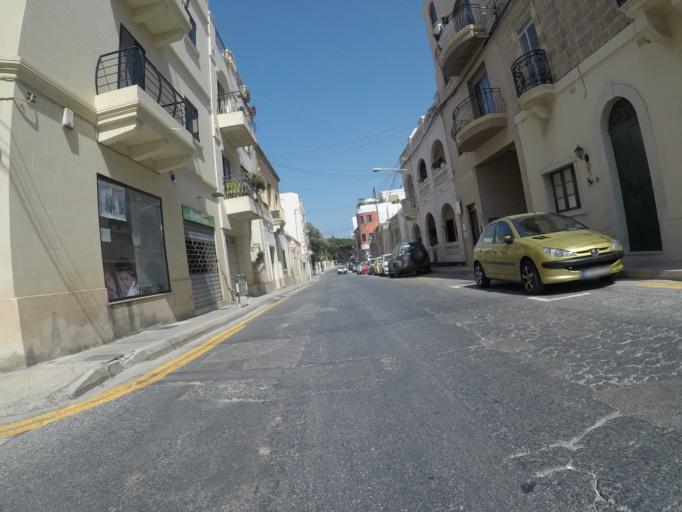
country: MT
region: L-Imgarr
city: Imgarr
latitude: 35.9194
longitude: 14.3679
